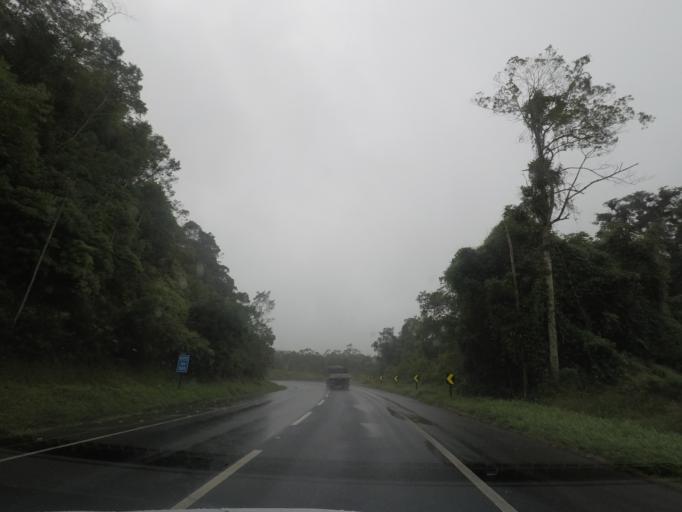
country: BR
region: Sao Paulo
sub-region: Cajati
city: Cajati
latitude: -24.9640
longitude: -48.4270
